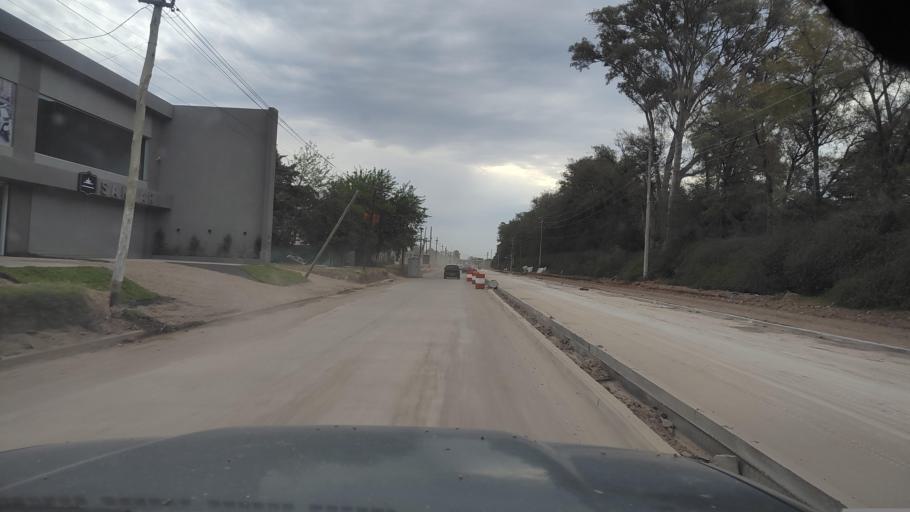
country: AR
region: Buenos Aires
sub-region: Partido de Lujan
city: Lujan
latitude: -34.5538
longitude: -59.0946
